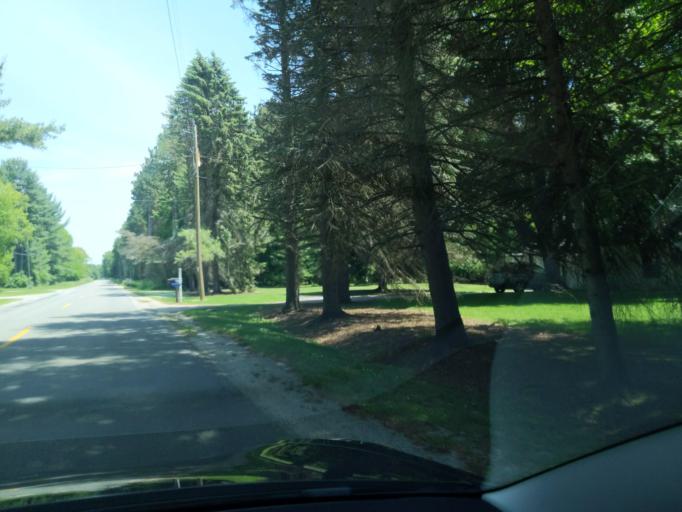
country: US
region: Michigan
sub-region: Muskegon County
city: Montague
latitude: 43.4161
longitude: -86.4146
